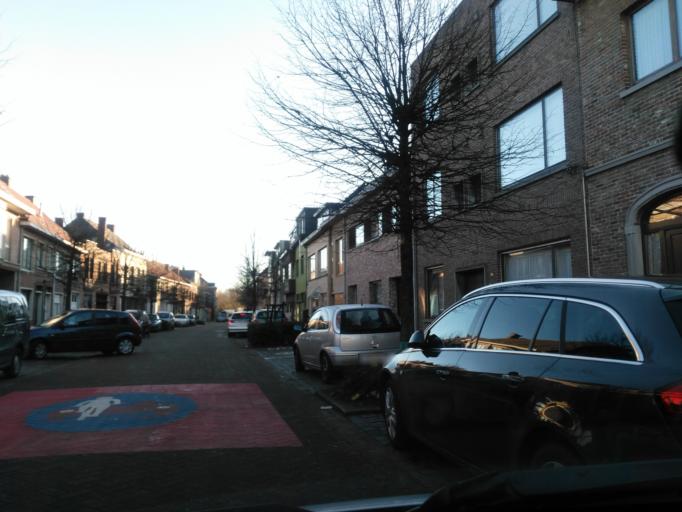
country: BE
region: Flanders
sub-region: Provincie Oost-Vlaanderen
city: Beveren
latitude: 51.2213
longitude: 4.2830
